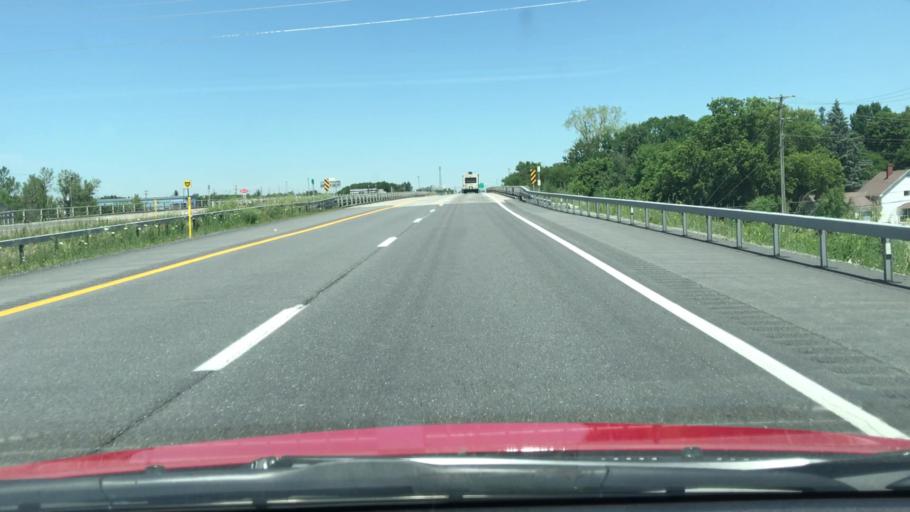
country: US
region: New York
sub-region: Clinton County
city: Champlain
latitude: 44.9904
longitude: -73.4567
